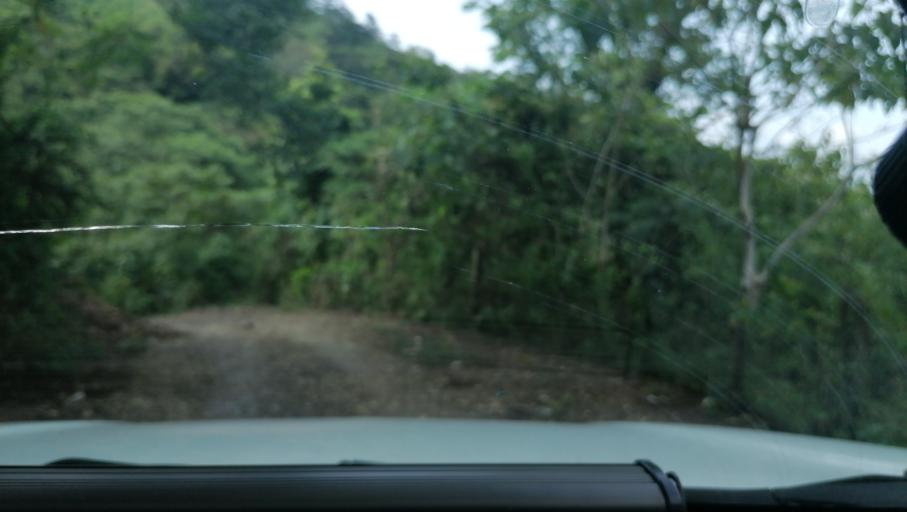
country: MX
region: Chiapas
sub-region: Tapilula
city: San Francisco Jacona
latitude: 17.3011
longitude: -93.1033
